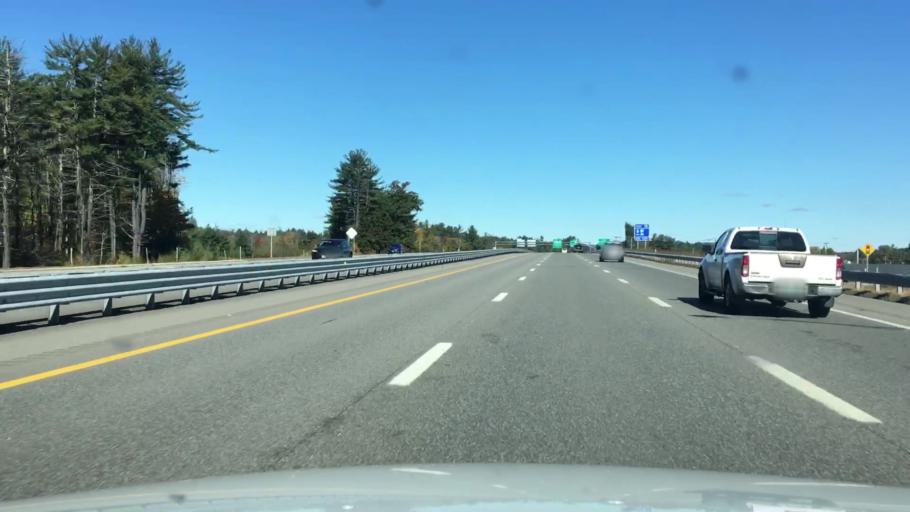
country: US
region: New Hampshire
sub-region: Strafford County
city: Rochester
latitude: 43.3101
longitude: -70.9958
